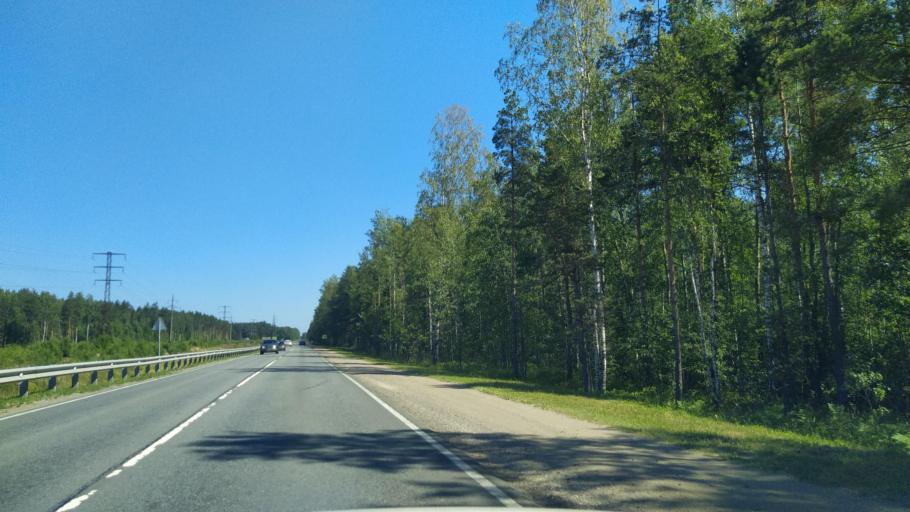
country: RU
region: Leningrad
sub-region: Volosovskiy Rayon
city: Shlissel'burg
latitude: 59.9559
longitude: 30.9984
